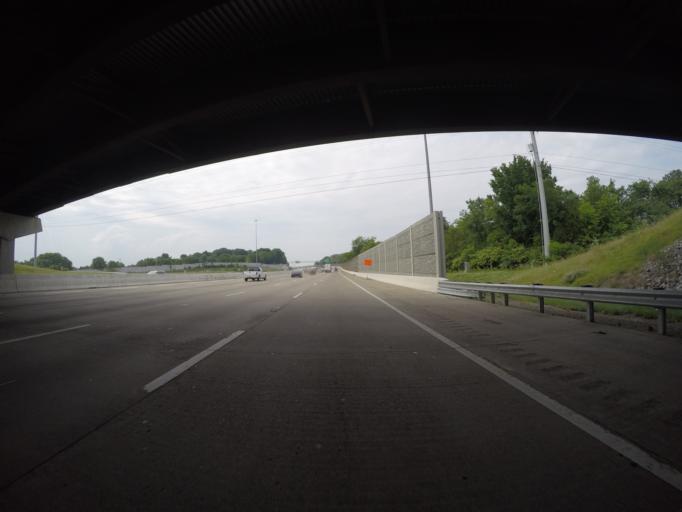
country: US
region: Tennessee
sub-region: Davidson County
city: Goodlettsville
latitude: 36.2650
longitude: -86.7377
